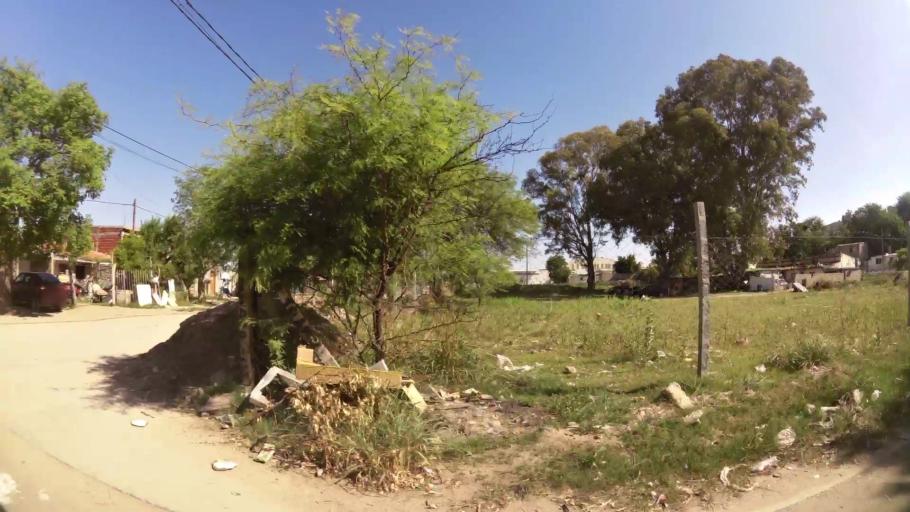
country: AR
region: Cordoba
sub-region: Departamento de Capital
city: Cordoba
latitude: -31.4106
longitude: -64.1453
